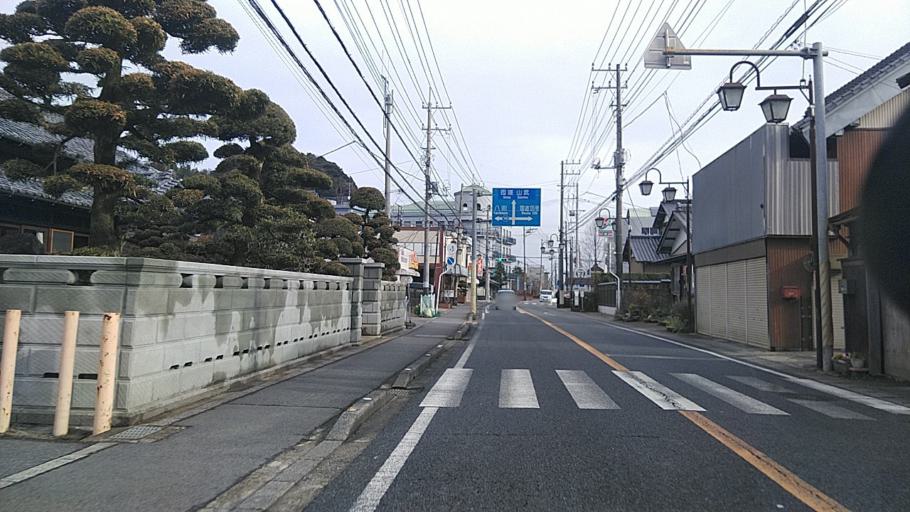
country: JP
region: Chiba
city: Togane
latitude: 35.5730
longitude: 140.3717
